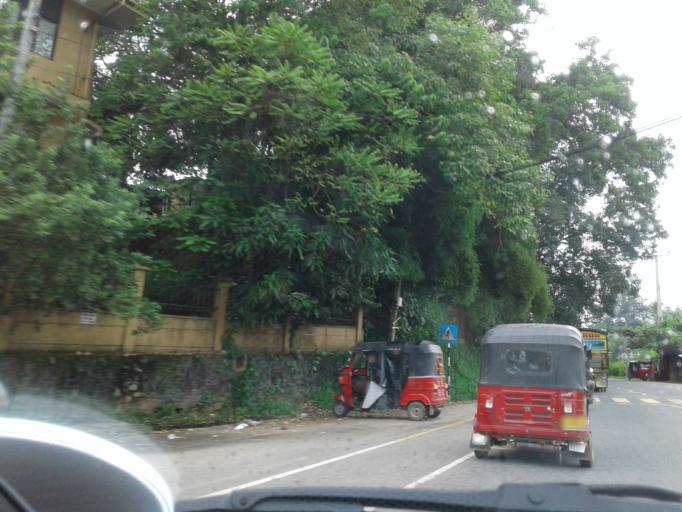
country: LK
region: Central
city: Kadugannawa
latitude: 7.2481
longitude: 80.3463
